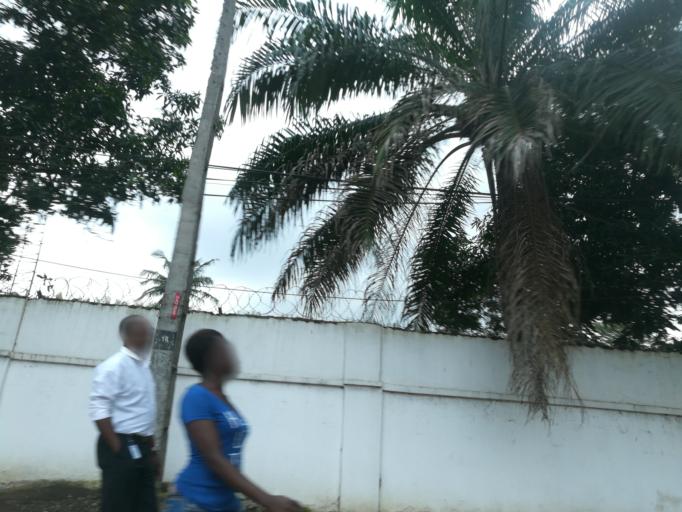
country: NG
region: Lagos
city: Agege
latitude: 6.6175
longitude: 3.3460
